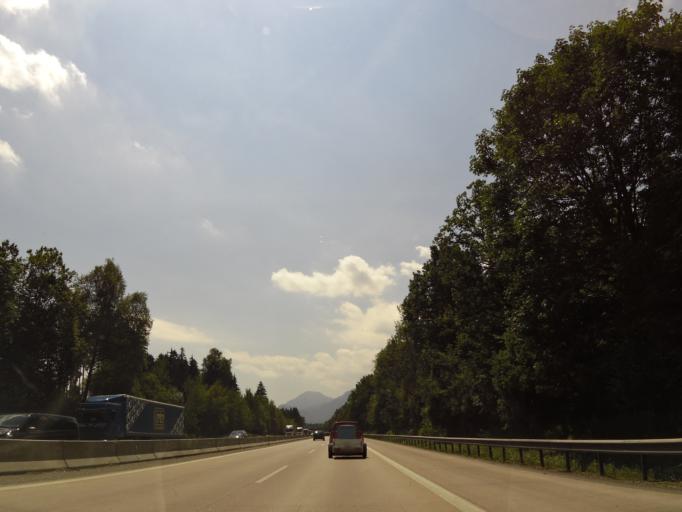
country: DE
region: Bavaria
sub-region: Upper Bavaria
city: Raubling
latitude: 47.7820
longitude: 12.0921
